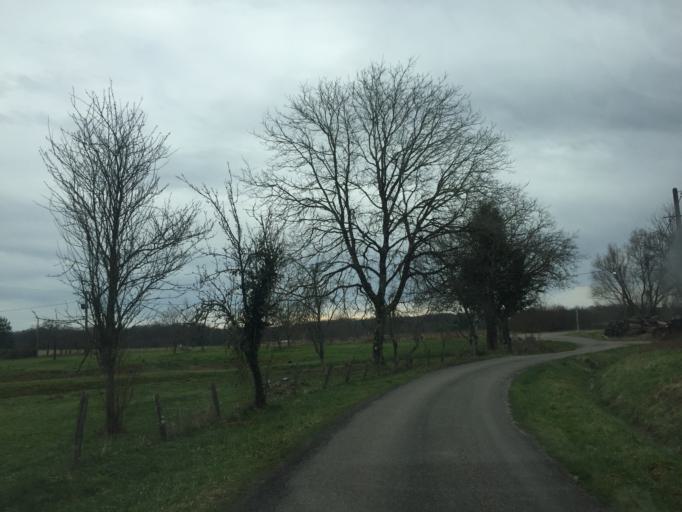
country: FR
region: Franche-Comte
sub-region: Departement du Jura
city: Mont-sous-Vaudrey
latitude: 46.8654
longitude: 5.5307
